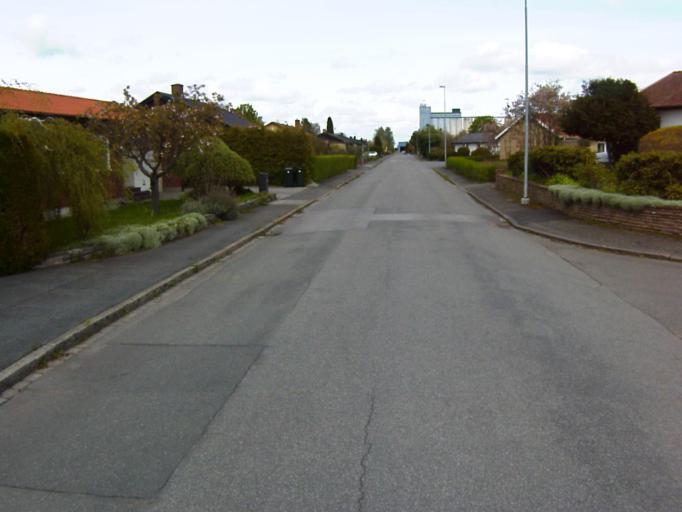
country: SE
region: Skane
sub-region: Kristianstads Kommun
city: Kristianstad
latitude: 56.0547
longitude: 14.1751
